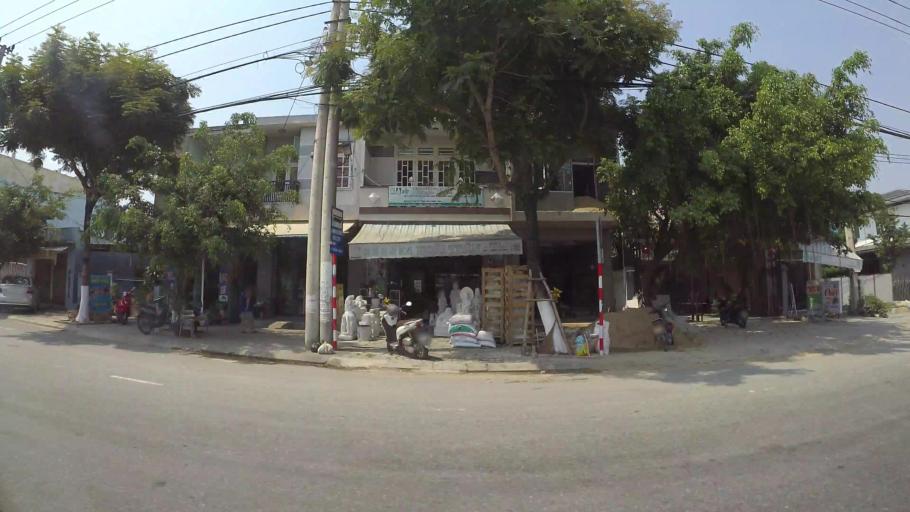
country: VN
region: Da Nang
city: Ngu Hanh Son
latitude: 16.0105
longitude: 108.2569
